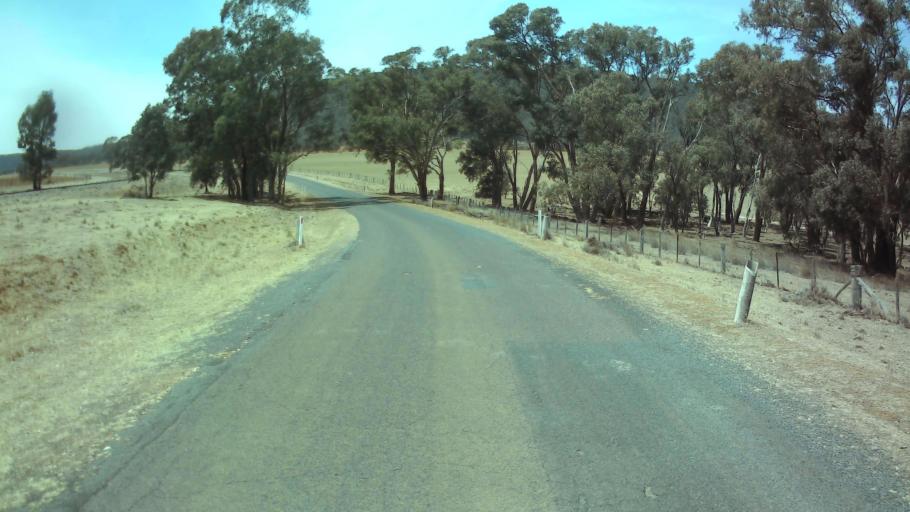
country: AU
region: New South Wales
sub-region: Weddin
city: Grenfell
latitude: -34.0348
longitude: 148.4347
